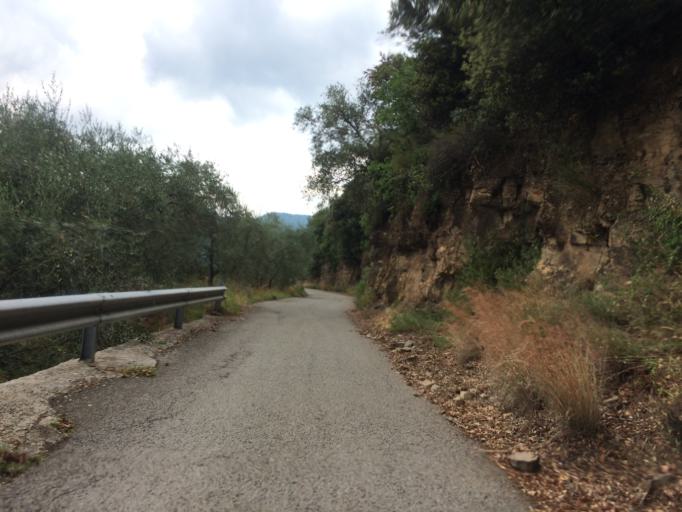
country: IT
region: Liguria
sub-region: Provincia di Imperia
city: Castel Vittorio
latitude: 43.9422
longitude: 7.6935
